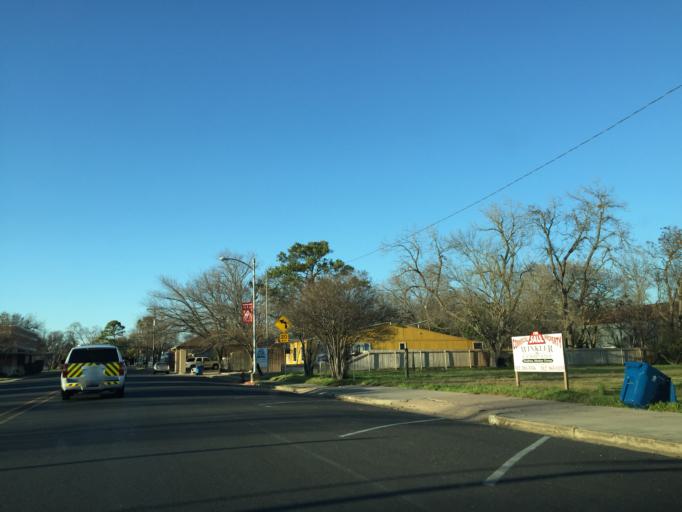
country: US
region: Texas
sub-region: Bastrop County
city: Elgin
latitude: 30.3500
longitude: -97.3714
